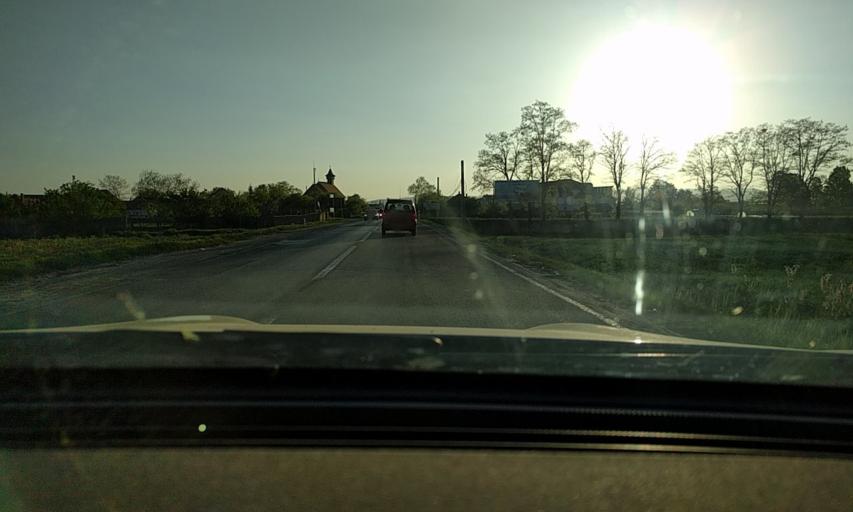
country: RO
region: Covasna
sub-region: Municipiul Targu Secuiesc
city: Targu Secuiesc
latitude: 45.9963
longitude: 26.1617
